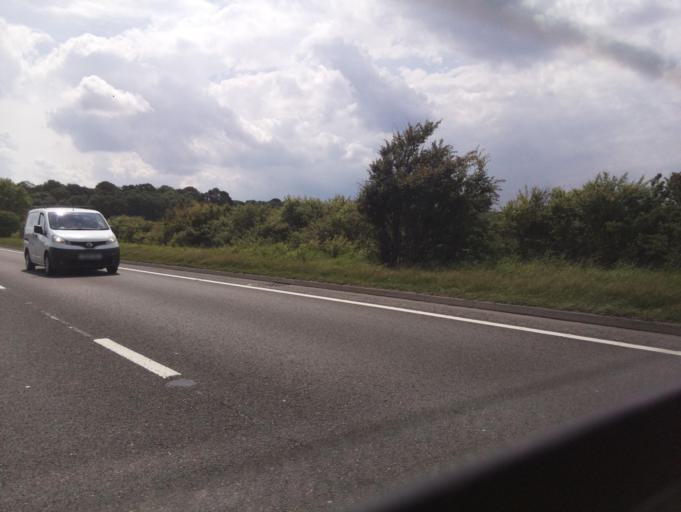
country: GB
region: England
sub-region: North Yorkshire
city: Northallerton
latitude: 54.3777
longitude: -1.3207
